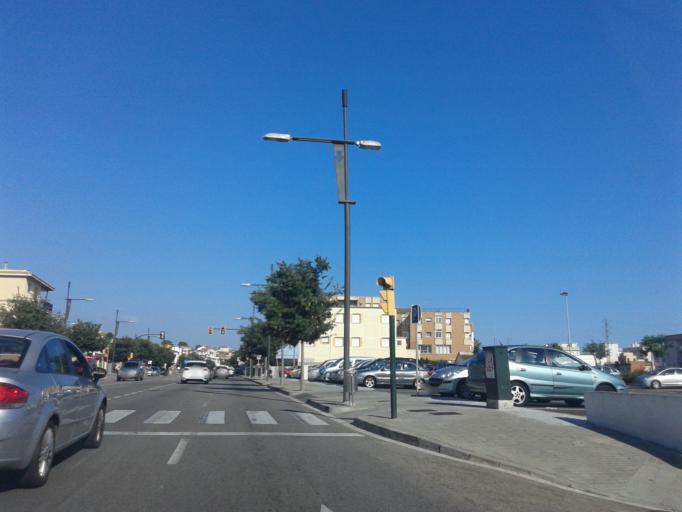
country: ES
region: Catalonia
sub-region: Provincia de Tarragona
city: Cunit
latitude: 41.1927
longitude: 1.6036
